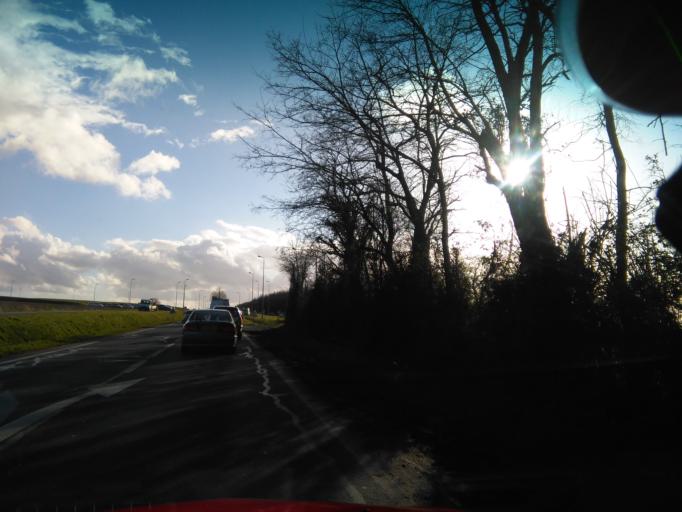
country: FR
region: Lower Normandy
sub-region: Departement du Calvados
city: Bretteville-sur-Odon
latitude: 49.1550
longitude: -0.4149
